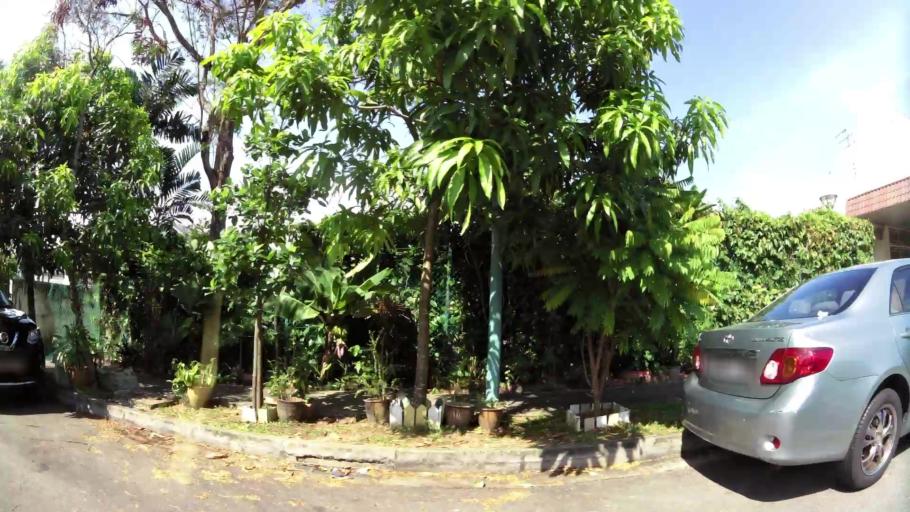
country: SG
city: Singapore
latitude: 1.3758
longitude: 103.8295
